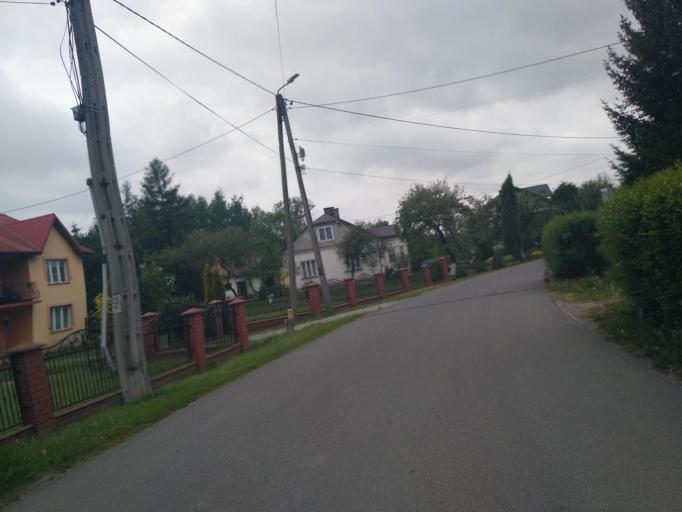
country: PL
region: Subcarpathian Voivodeship
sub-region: Powiat krosnienski
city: Chorkowka
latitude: 49.6672
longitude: 21.7084
